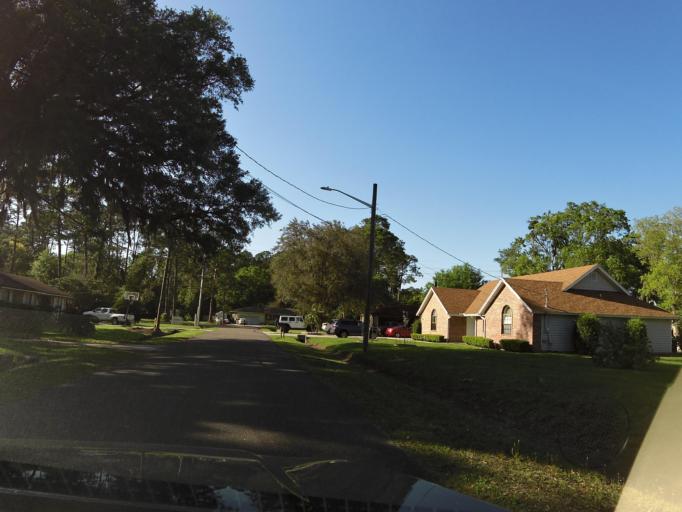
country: US
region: Florida
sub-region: Duval County
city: Jacksonville
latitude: 30.2794
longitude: -81.5843
